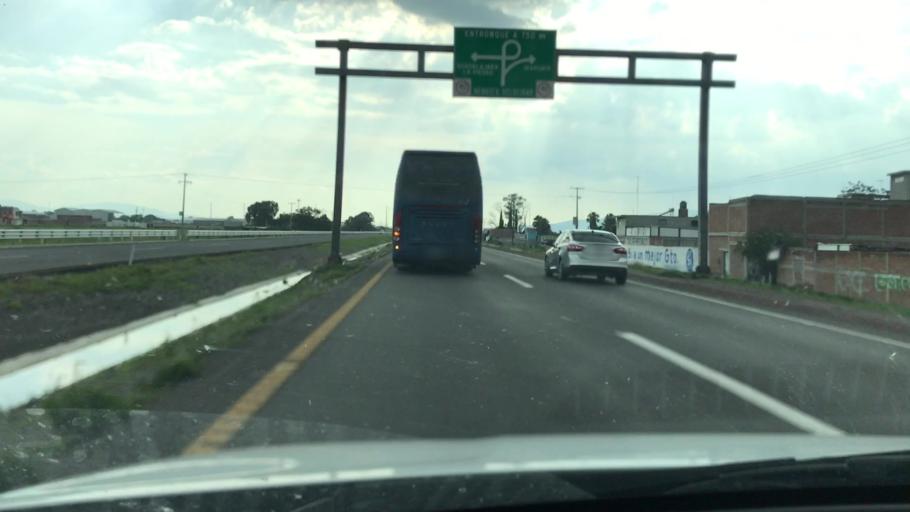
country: MX
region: Guanajuato
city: Irapuato
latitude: 20.6495
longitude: -101.3635
